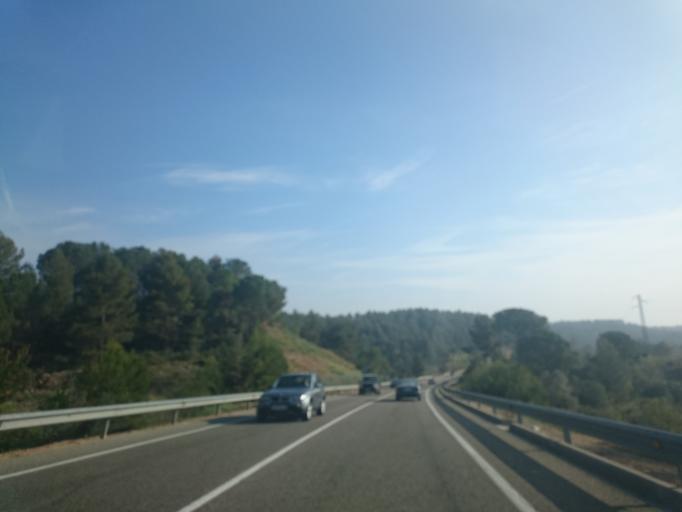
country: ES
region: Catalonia
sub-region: Provincia de Barcelona
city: Sant Salvador de Guardiola
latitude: 41.6851
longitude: 1.7557
